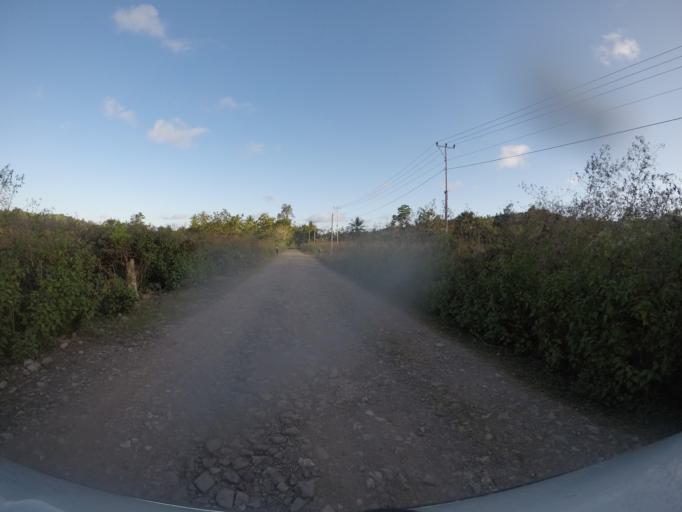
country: TL
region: Baucau
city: Venilale
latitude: -8.7292
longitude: 126.7088
